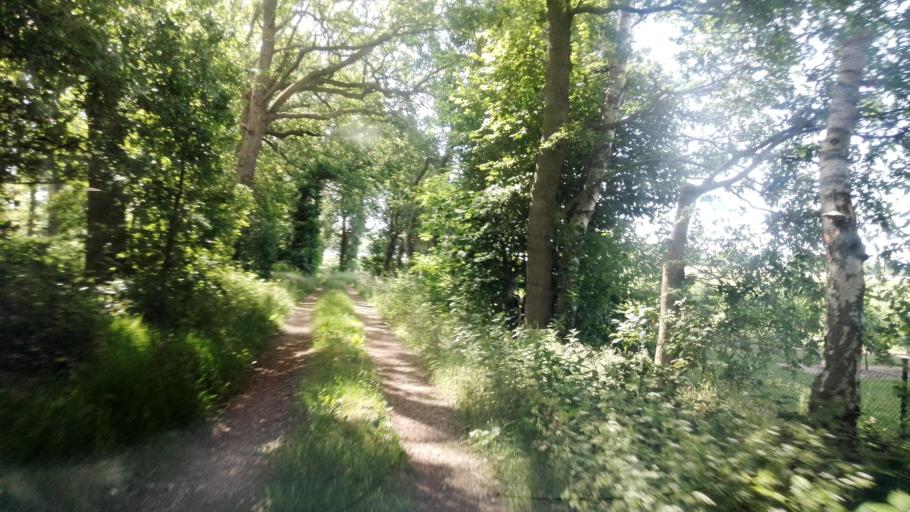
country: NL
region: Limburg
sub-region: Gemeente Venray
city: Venray
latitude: 51.4740
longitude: 6.0536
